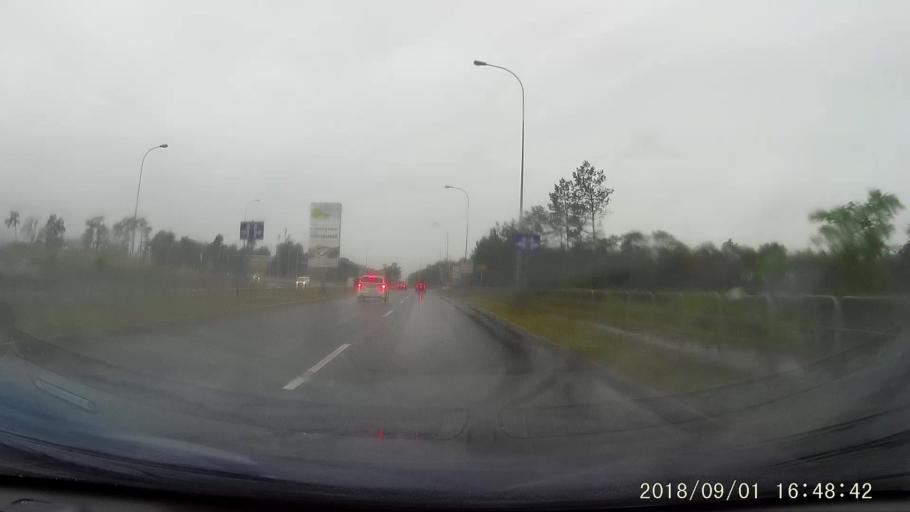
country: PL
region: Lubusz
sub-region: Zielona Gora
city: Zielona Gora
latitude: 51.9583
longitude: 15.5280
